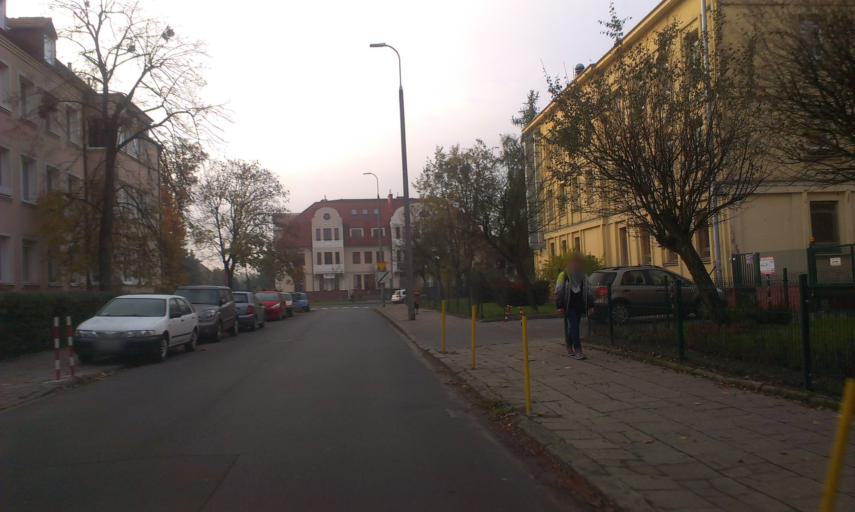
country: PL
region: Greater Poland Voivodeship
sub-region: Poznan
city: Poznan
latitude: 52.4051
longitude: 16.8778
